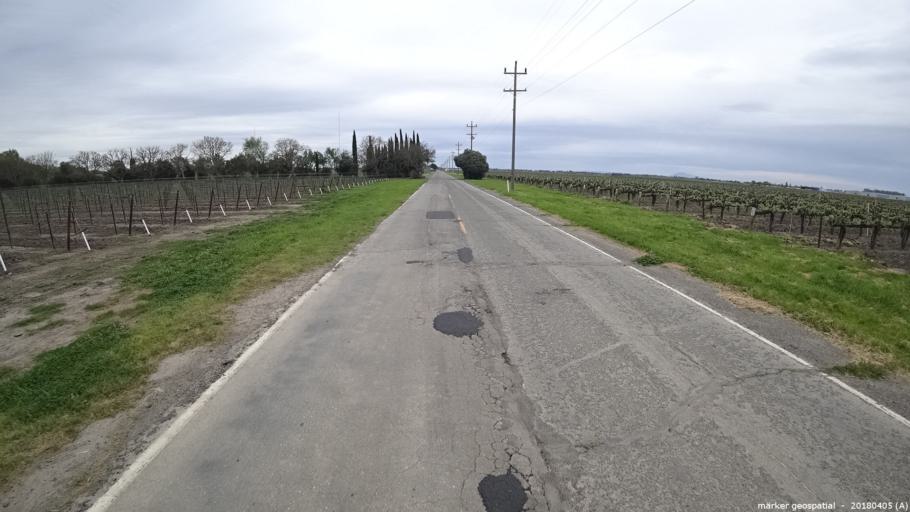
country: US
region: California
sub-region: Sacramento County
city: Walnut Grove
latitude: 38.3066
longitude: -121.5172
